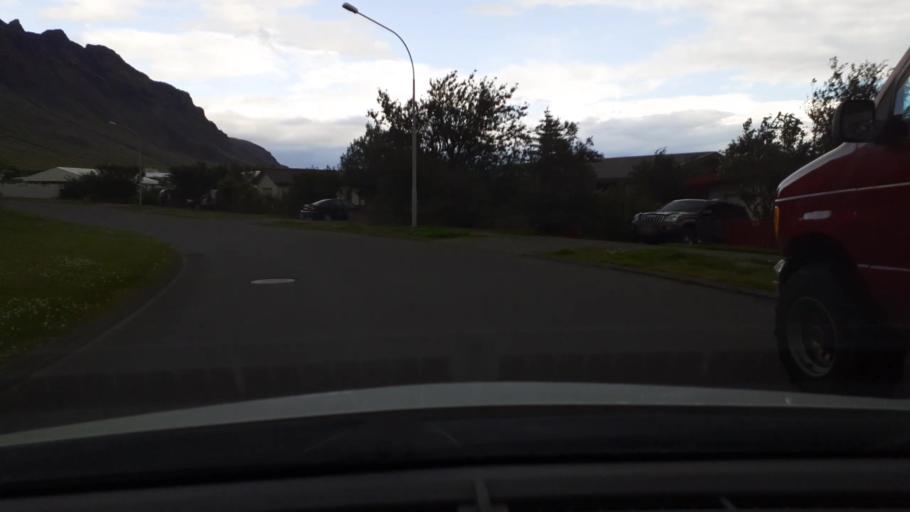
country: IS
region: Capital Region
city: Reykjavik
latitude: 64.2393
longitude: -21.8348
